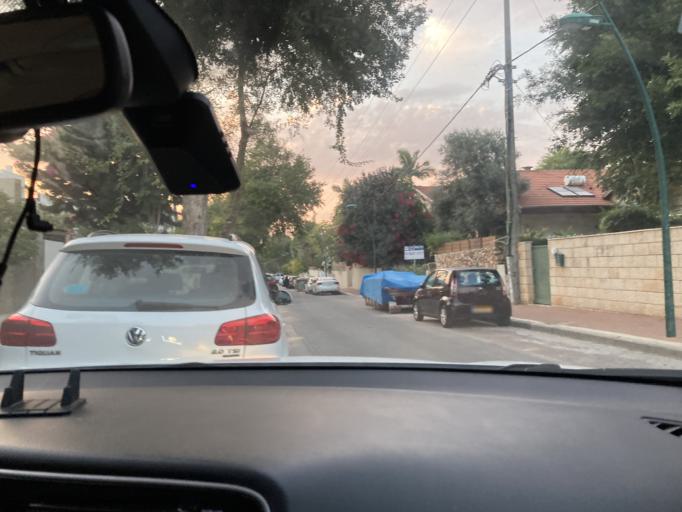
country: IL
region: Tel Aviv
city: Ramat HaSharon
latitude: 32.1516
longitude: 34.8325
